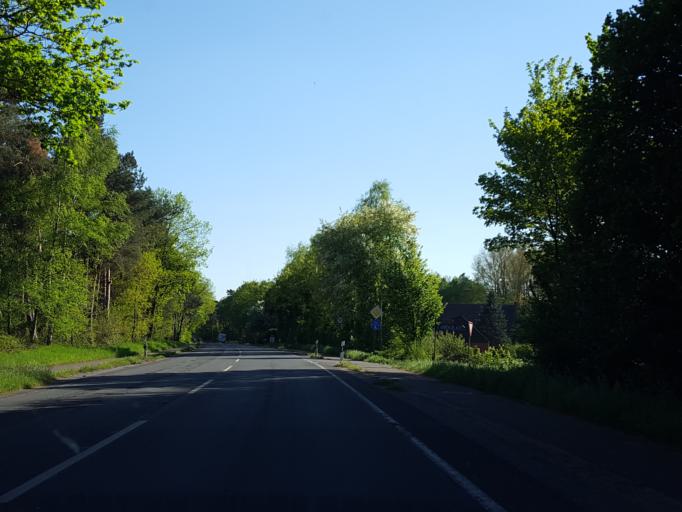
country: DE
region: North Rhine-Westphalia
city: Oer-Erkenschwick
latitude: 51.6901
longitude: 7.2977
